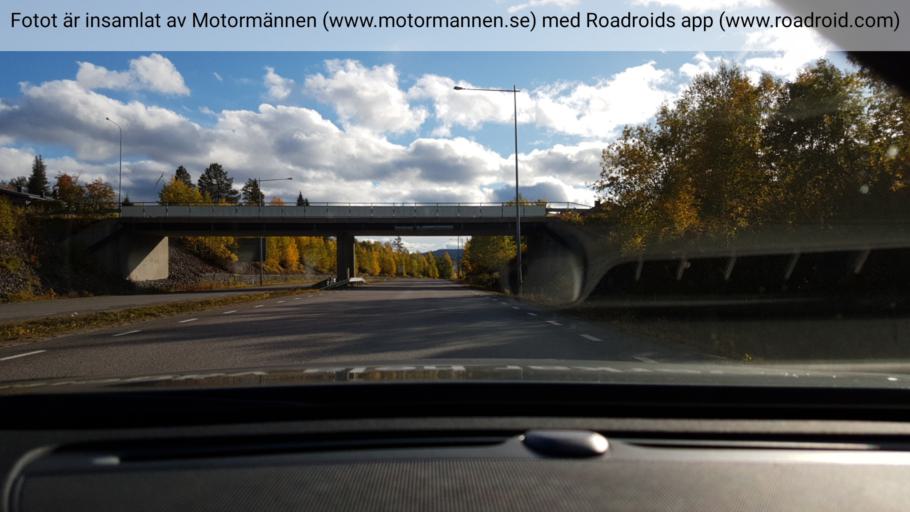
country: SE
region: Norrbotten
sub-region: Gallivare Kommun
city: Gaellivare
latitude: 67.1426
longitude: 20.6626
